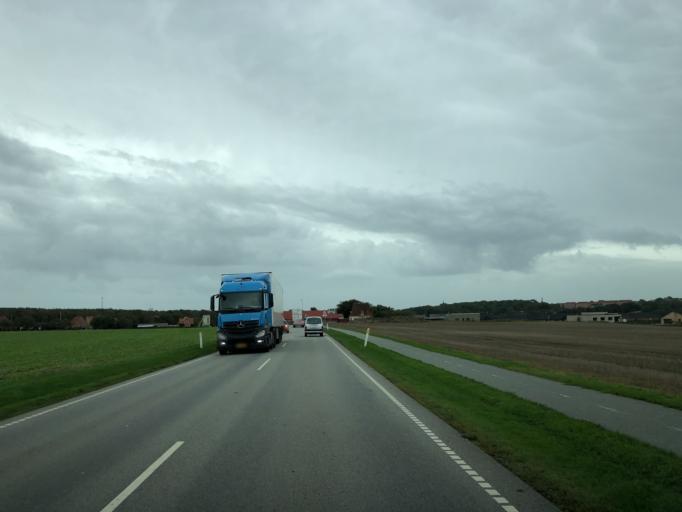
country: DK
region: North Denmark
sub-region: Thisted Kommune
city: Thisted
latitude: 56.9695
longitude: 8.6862
